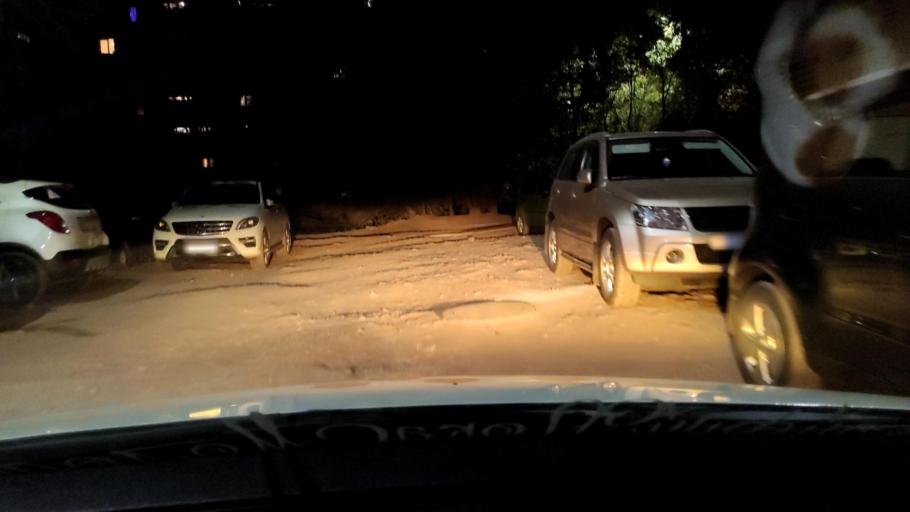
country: RU
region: Voronezj
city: Podgornoye
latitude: 51.6998
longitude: 39.1410
